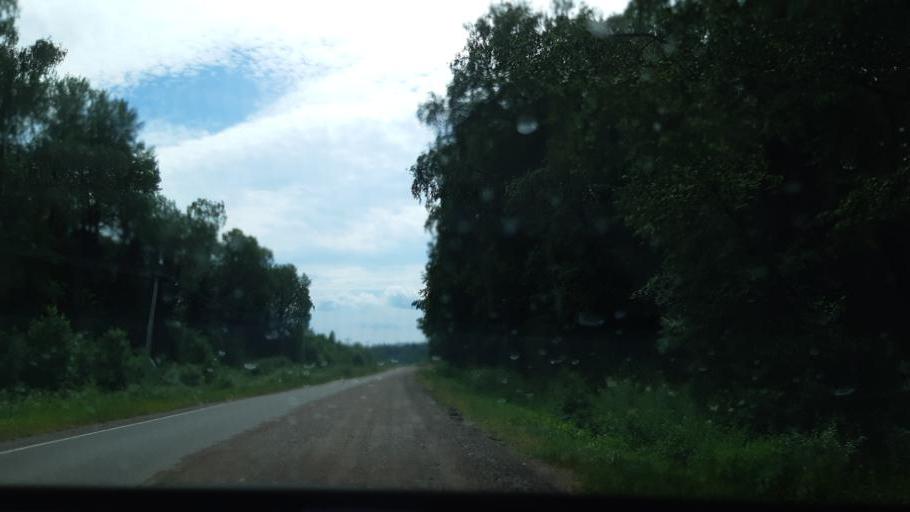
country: RU
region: Moskovskaya
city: Vereya
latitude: 55.2454
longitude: 36.0488
